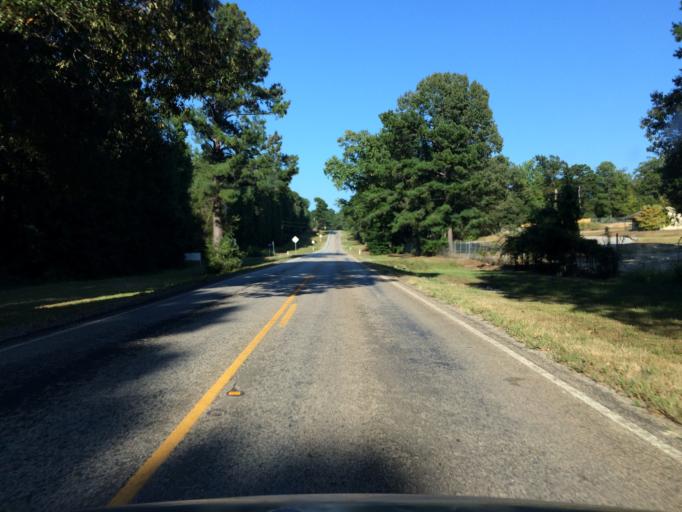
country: US
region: Texas
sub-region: Wood County
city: Hawkins
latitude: 32.6391
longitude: -95.2566
